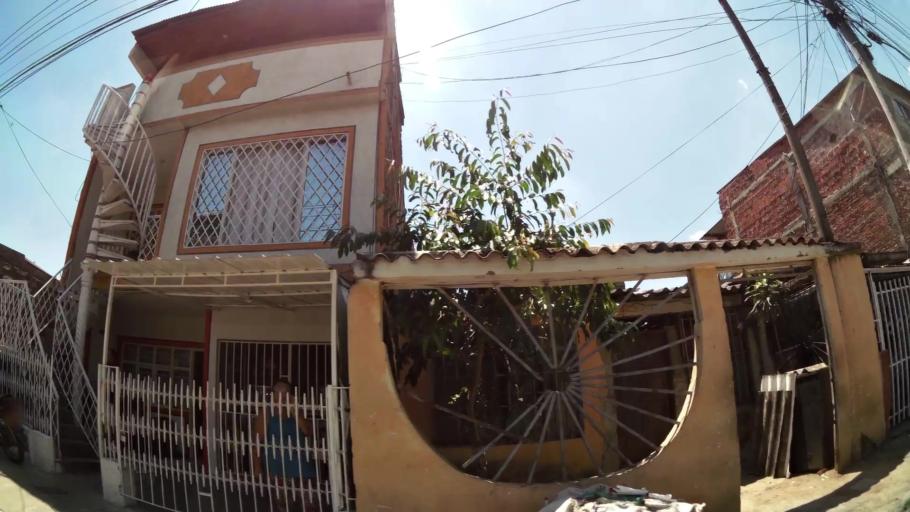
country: CO
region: Valle del Cauca
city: Cali
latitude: 3.4337
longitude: -76.5070
